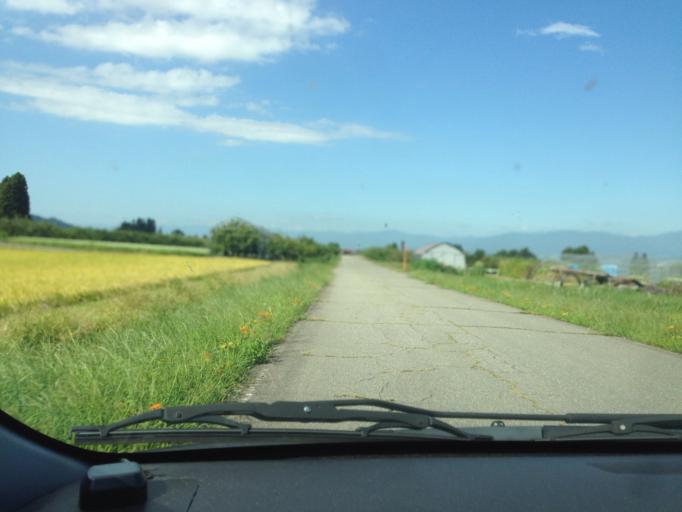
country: JP
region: Fukushima
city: Kitakata
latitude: 37.4376
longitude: 139.8095
